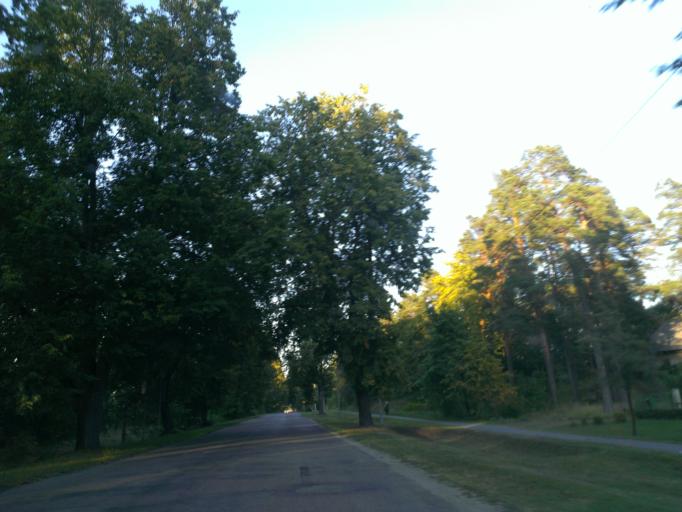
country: LV
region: Garkalne
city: Garkalne
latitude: 57.0475
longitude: 24.4242
